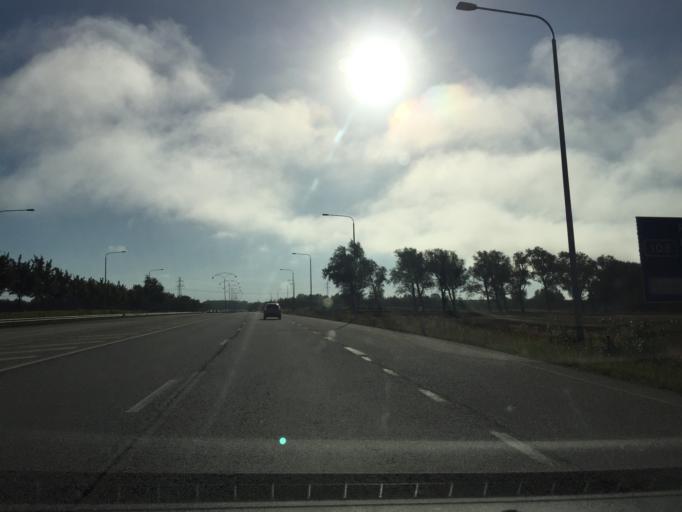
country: SE
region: Skane
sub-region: Lunds Kommun
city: Lund
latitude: 55.7198
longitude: 13.1456
